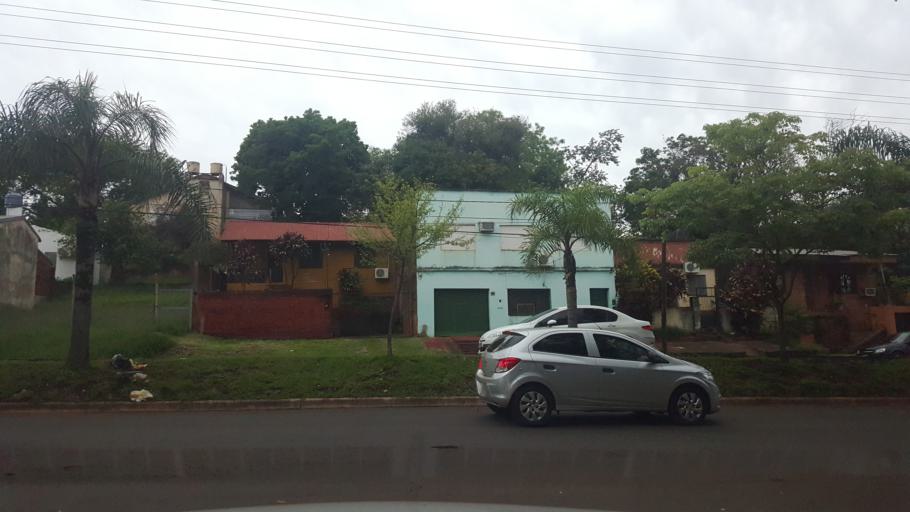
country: AR
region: Misiones
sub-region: Departamento de Capital
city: Posadas
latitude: -27.3596
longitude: -55.9070
